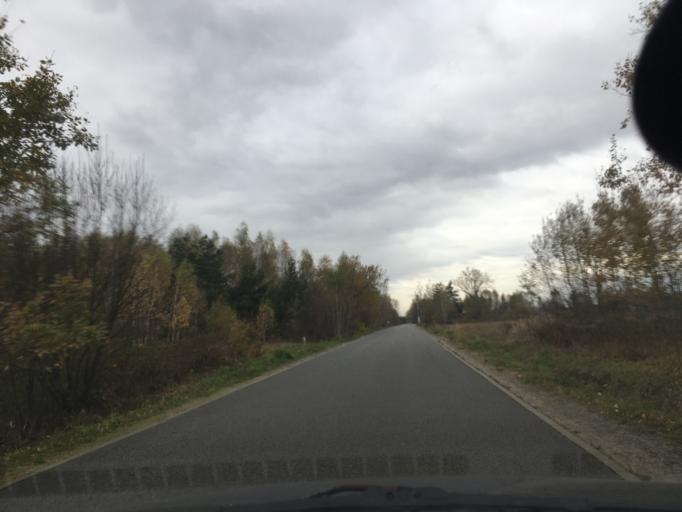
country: PL
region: Lodz Voivodeship
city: Zabia Wola
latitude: 52.0226
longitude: 20.7149
